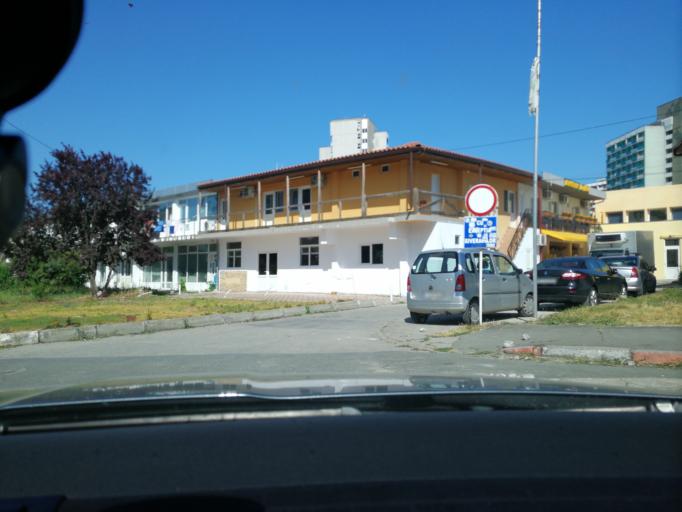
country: RO
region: Constanta
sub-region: Municipiul Mangalia
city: Mangalia
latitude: 43.8306
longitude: 28.5867
